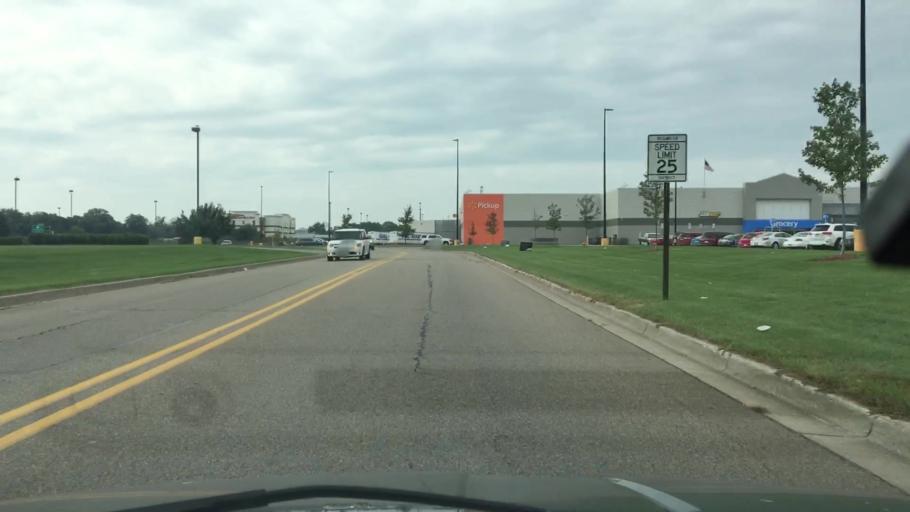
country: US
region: Michigan
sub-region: Berrien County
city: Fair Plain
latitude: 42.0776
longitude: -86.4231
